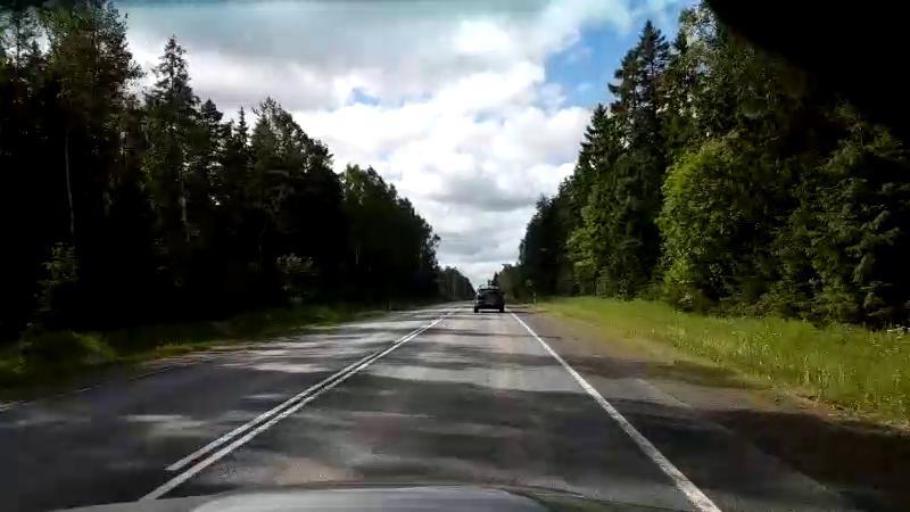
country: EE
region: Harju
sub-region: Saue linn
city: Saue
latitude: 59.2042
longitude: 24.4974
